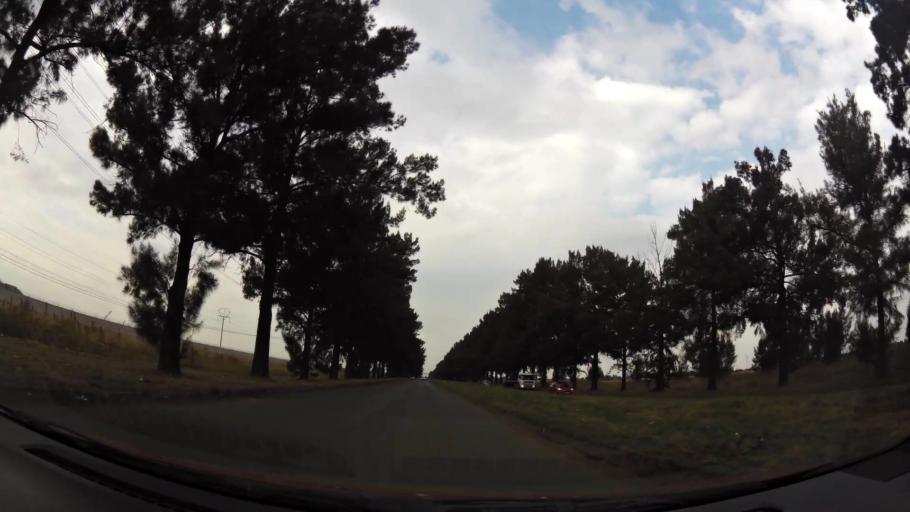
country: ZA
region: Gauteng
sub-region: Sedibeng District Municipality
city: Vanderbijlpark
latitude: -26.6741
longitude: 27.8231
